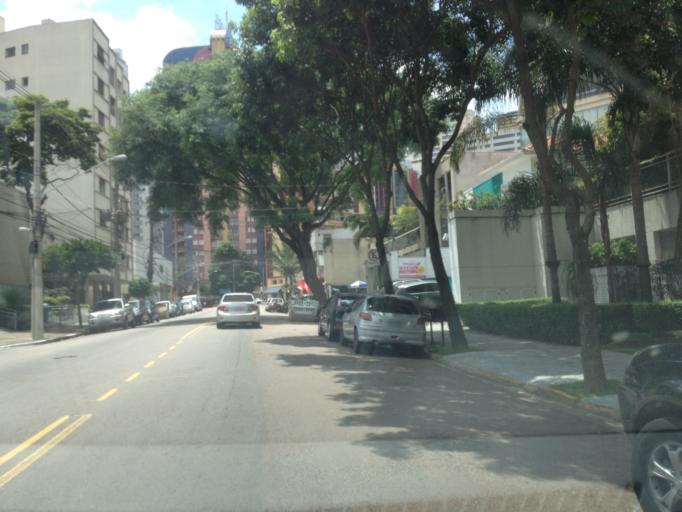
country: BR
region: Sao Paulo
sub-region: Sao Paulo
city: Sao Paulo
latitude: -23.5754
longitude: -46.6507
